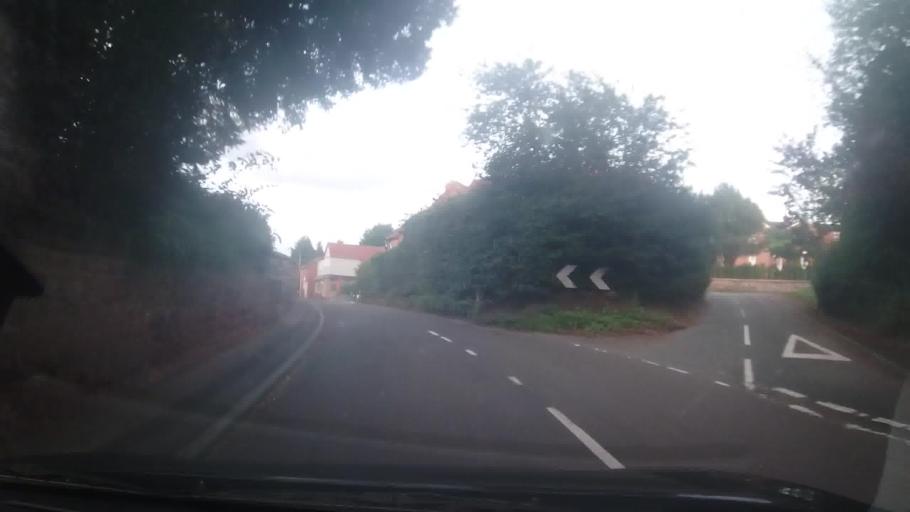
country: GB
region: England
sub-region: Shropshire
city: Great Ness
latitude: 52.7933
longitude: -2.8984
